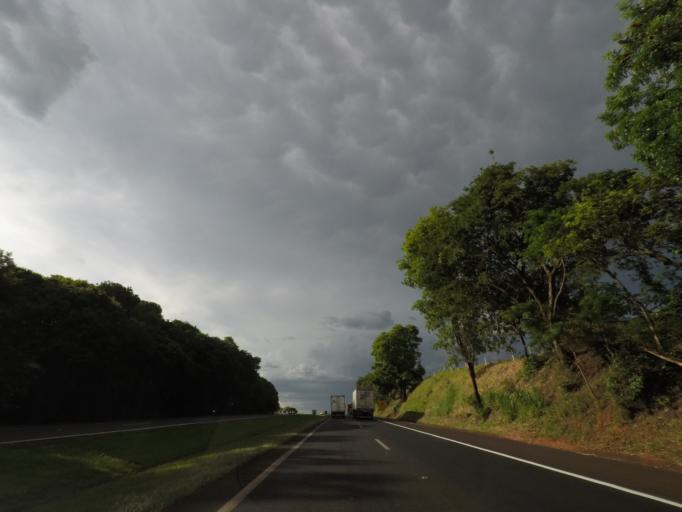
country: BR
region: Sao Paulo
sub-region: Jardinopolis
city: Jardinopolis
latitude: -21.0596
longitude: -47.8200
